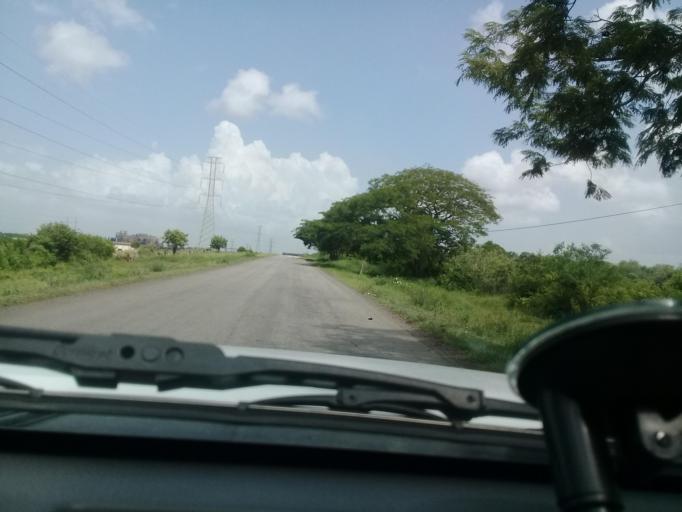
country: MX
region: Veracruz
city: Moralillo
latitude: 22.2268
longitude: -98.0130
